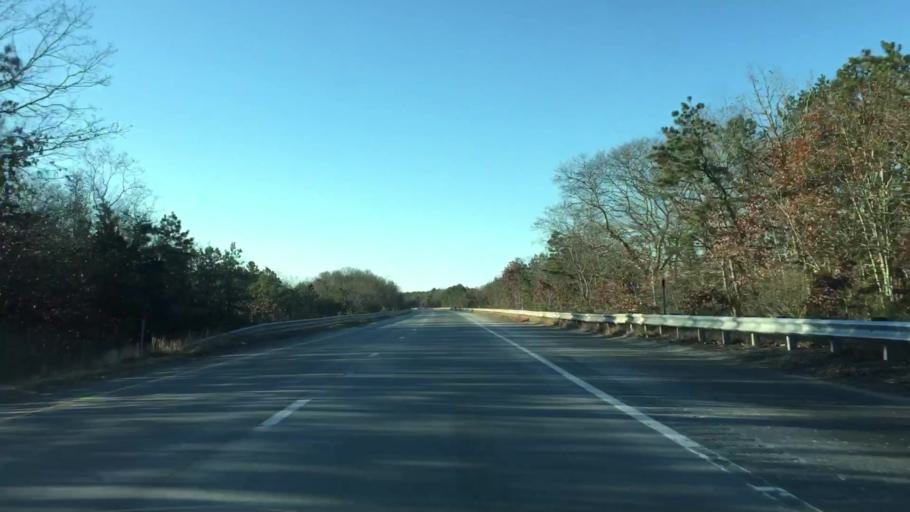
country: US
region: Massachusetts
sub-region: Barnstable County
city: Pocasset
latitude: 41.6798
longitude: -70.5946
